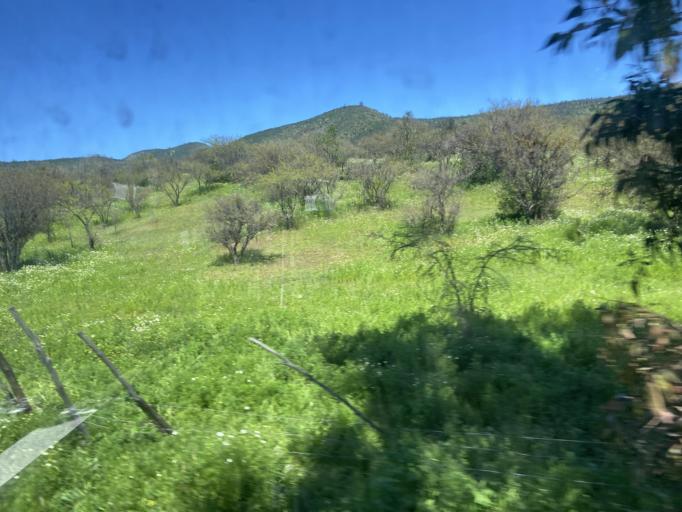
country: CL
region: Valparaiso
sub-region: Provincia de Marga Marga
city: Villa Alemana
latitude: -33.1662
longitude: -71.3148
